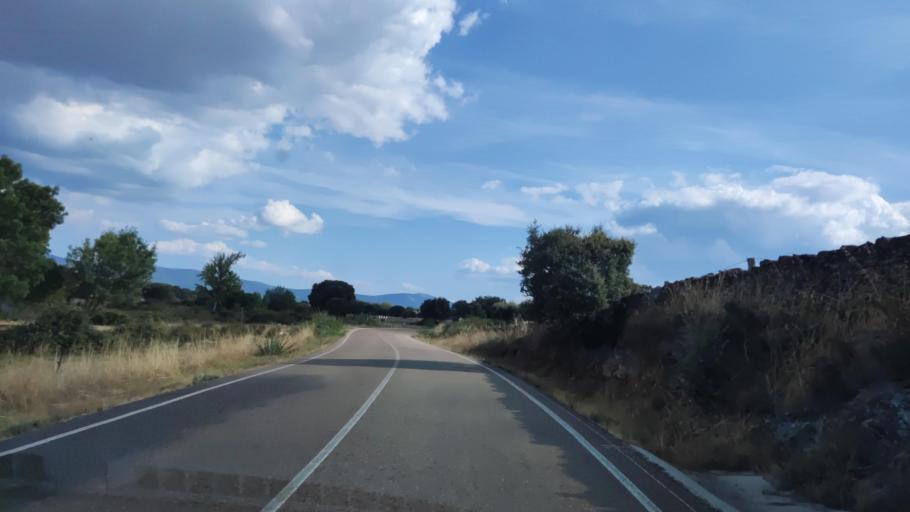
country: ES
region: Castille and Leon
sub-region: Provincia de Salamanca
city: Martiago
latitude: 40.4705
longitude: -6.4897
